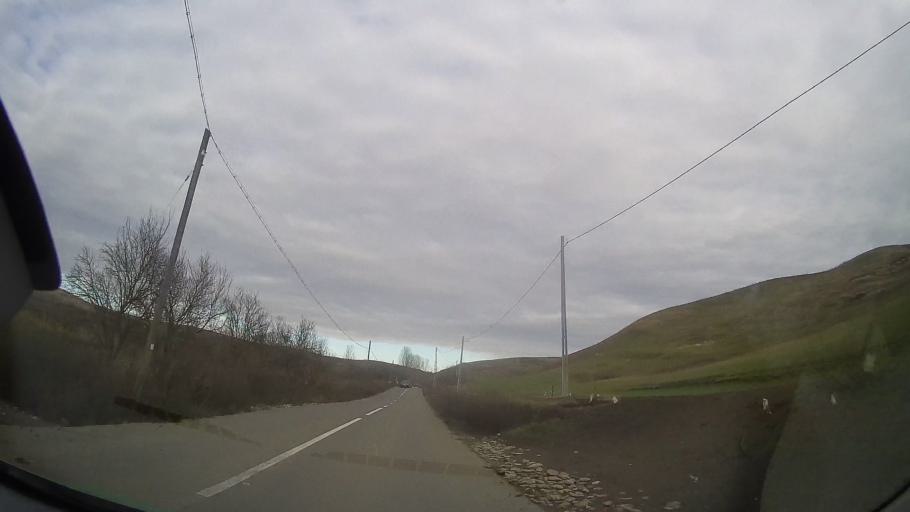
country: RO
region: Bistrita-Nasaud
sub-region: Comuna Silvasu de Campie
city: Silvasu de Campie
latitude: 46.8102
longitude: 24.2950
